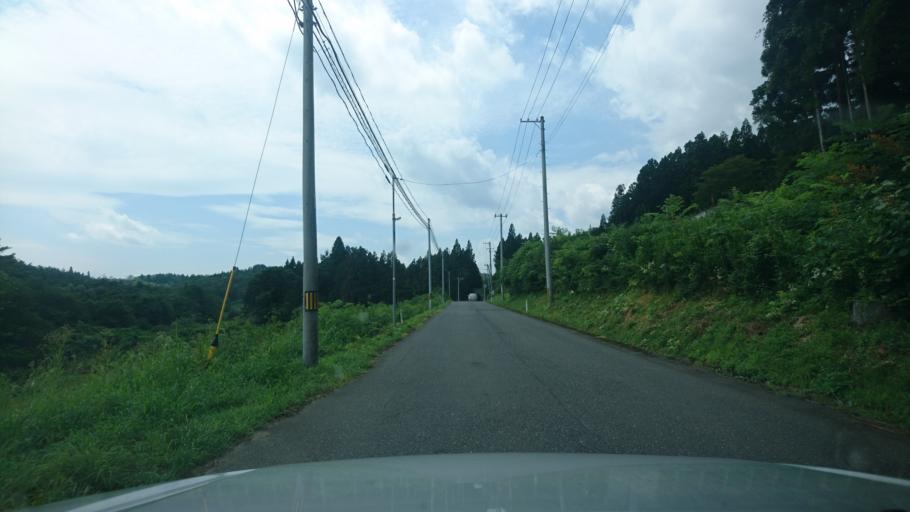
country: JP
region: Iwate
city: Ichinoseki
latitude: 38.8149
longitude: 140.9280
